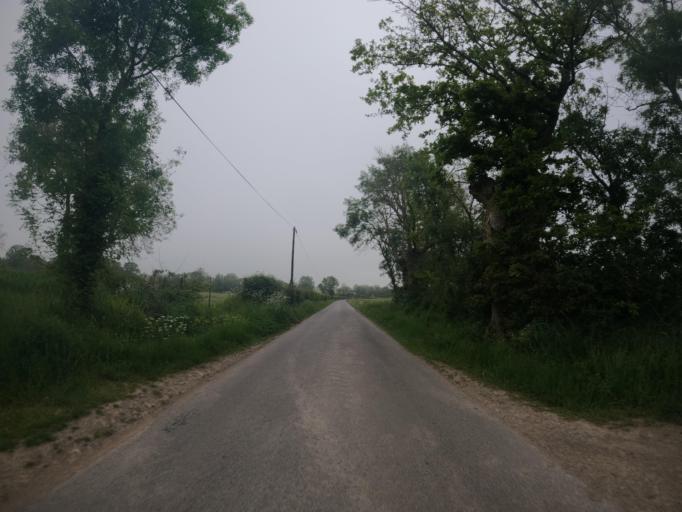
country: FR
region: Poitou-Charentes
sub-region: Departement des Deux-Sevres
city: Chiche
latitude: 46.8719
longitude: -0.3360
